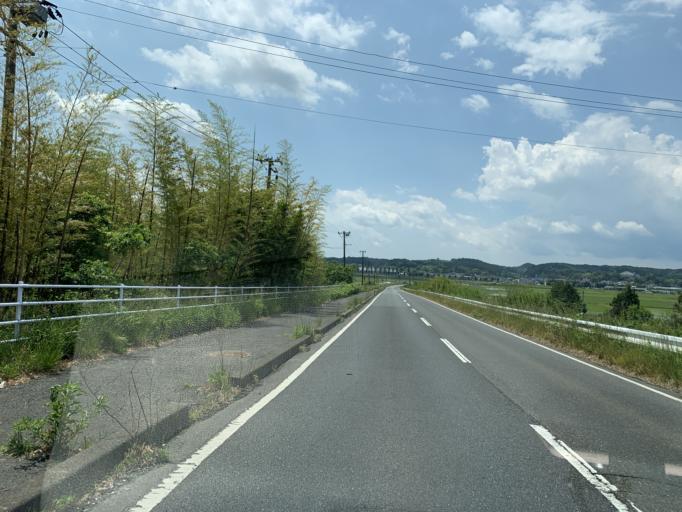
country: JP
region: Miyagi
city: Kogota
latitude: 38.5264
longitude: 141.0580
